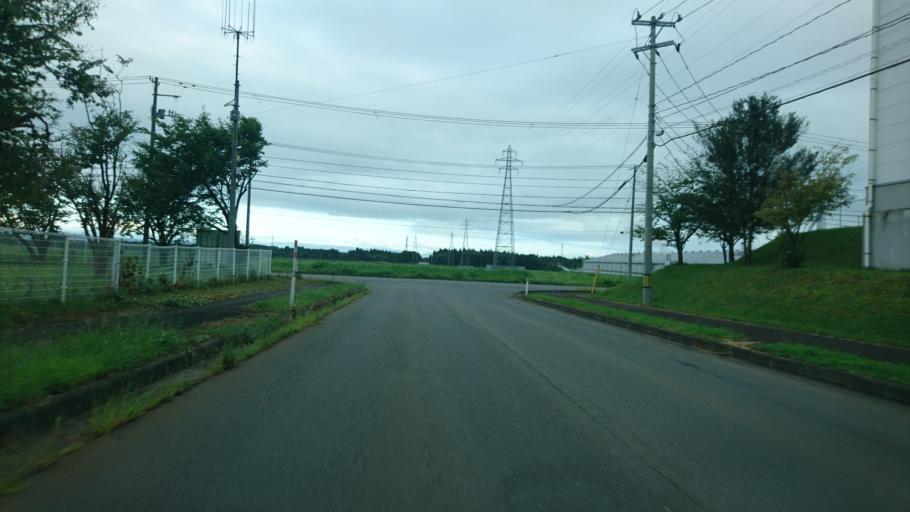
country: JP
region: Iwate
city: Kitakami
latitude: 39.3274
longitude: 141.0070
